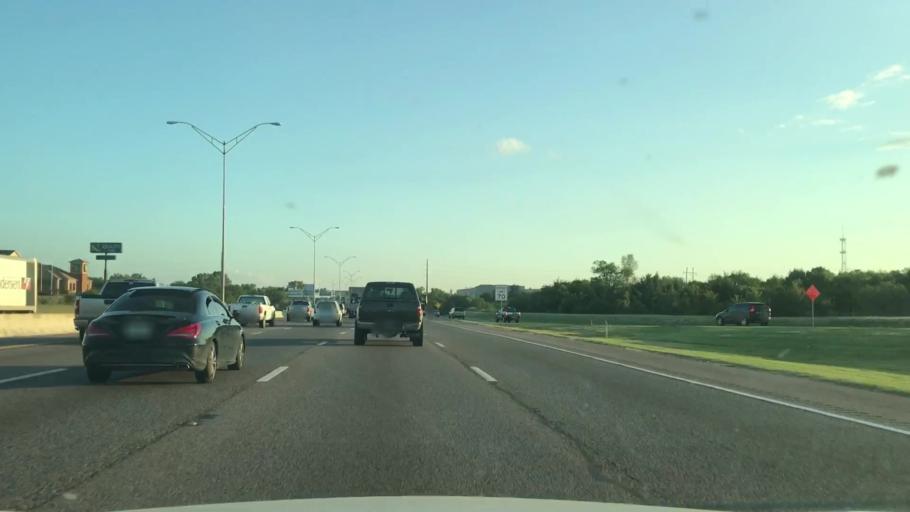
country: US
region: Texas
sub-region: Dallas County
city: Mesquite
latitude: 32.7797
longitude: -96.6244
